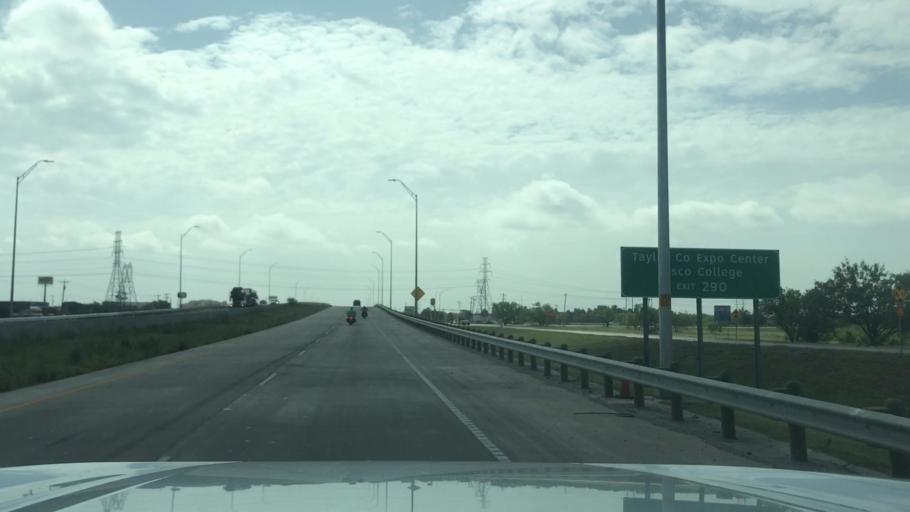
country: US
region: Texas
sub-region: Taylor County
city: Abilene
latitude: 32.4793
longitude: -99.7027
